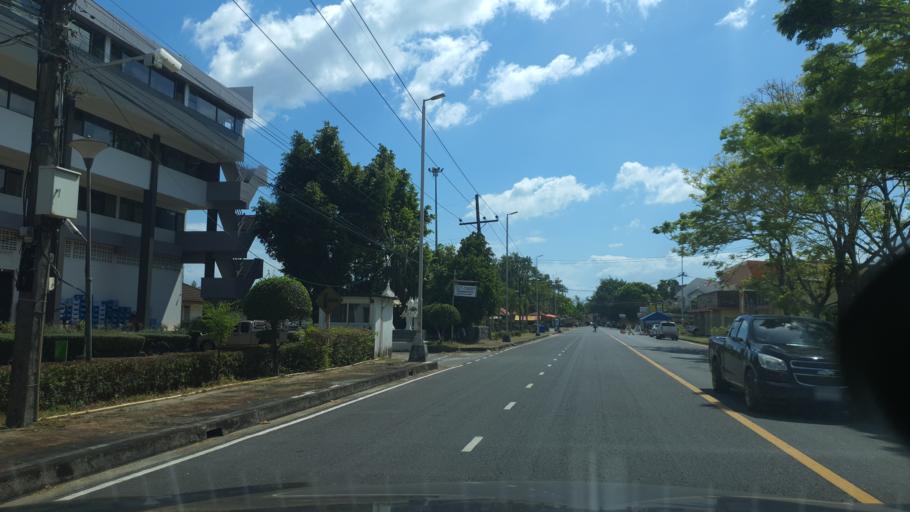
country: TH
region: Phangnga
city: Phang Nga
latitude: 8.3990
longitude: 98.5133
